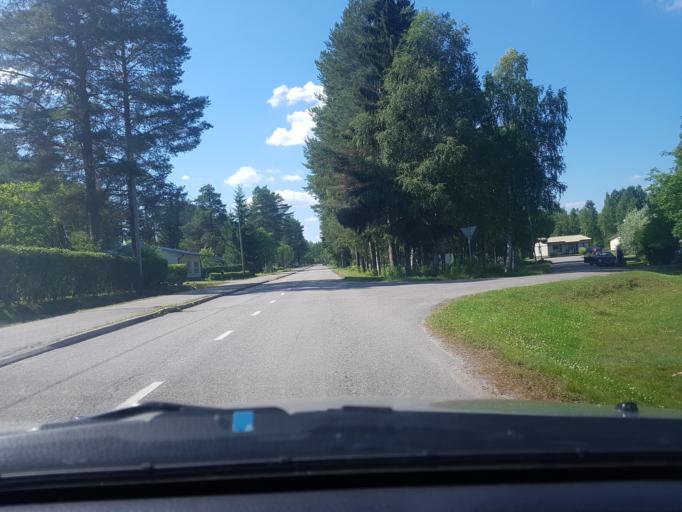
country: FI
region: Kainuu
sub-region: Kehys-Kainuu
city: Kuhmo
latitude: 64.1213
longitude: 29.5275
